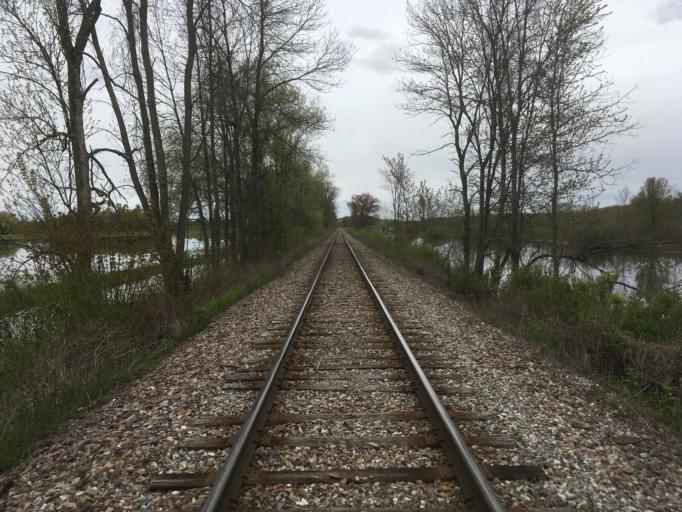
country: US
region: Vermont
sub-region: Addison County
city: Middlebury (village)
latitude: 43.9562
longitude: -73.1622
